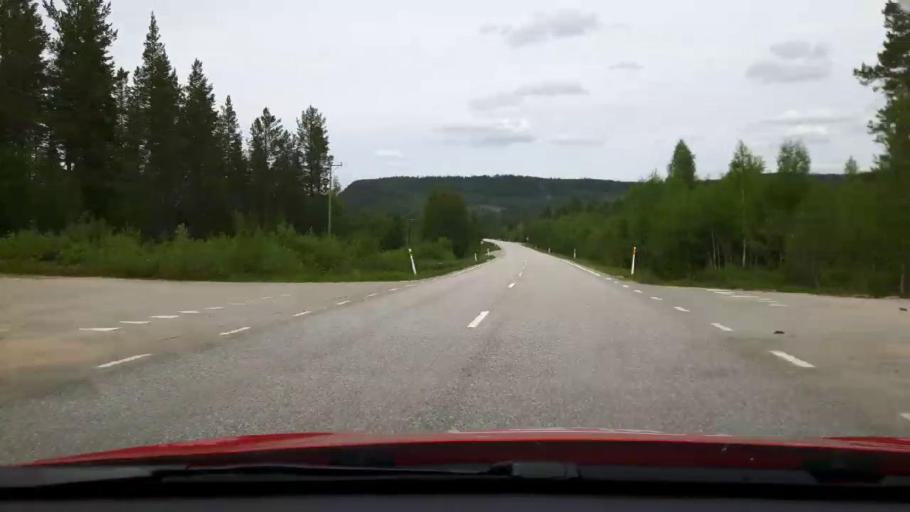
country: SE
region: Jaemtland
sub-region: Harjedalens Kommun
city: Sveg
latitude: 62.0886
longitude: 14.2483
